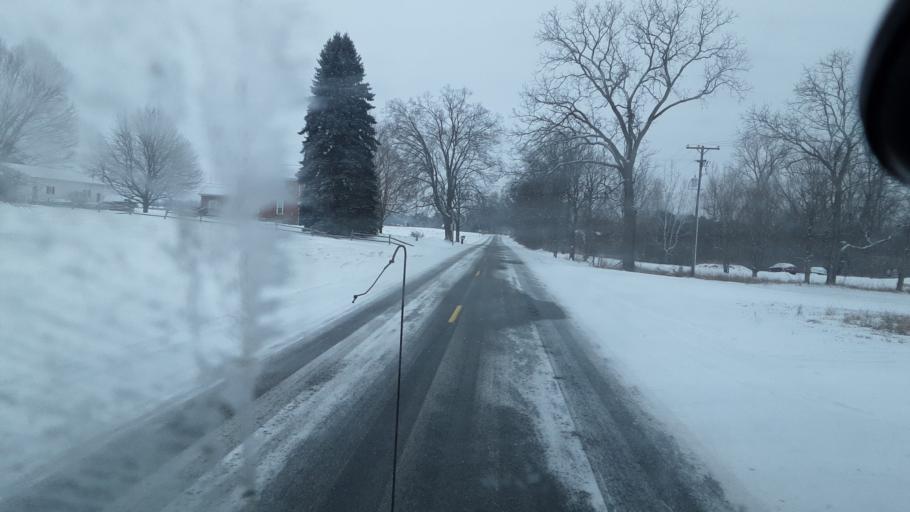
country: US
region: Michigan
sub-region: Ingham County
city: Leslie
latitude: 42.4295
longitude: -84.3168
